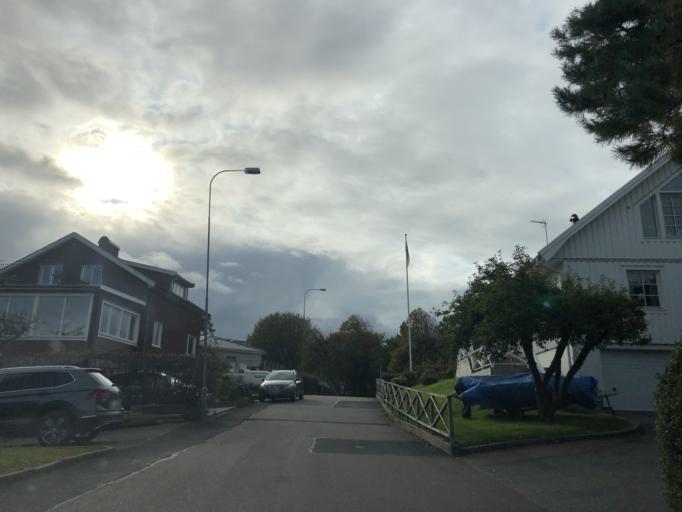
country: SE
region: Vaestra Goetaland
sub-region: Goteborg
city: Majorna
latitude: 57.6774
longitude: 11.8772
